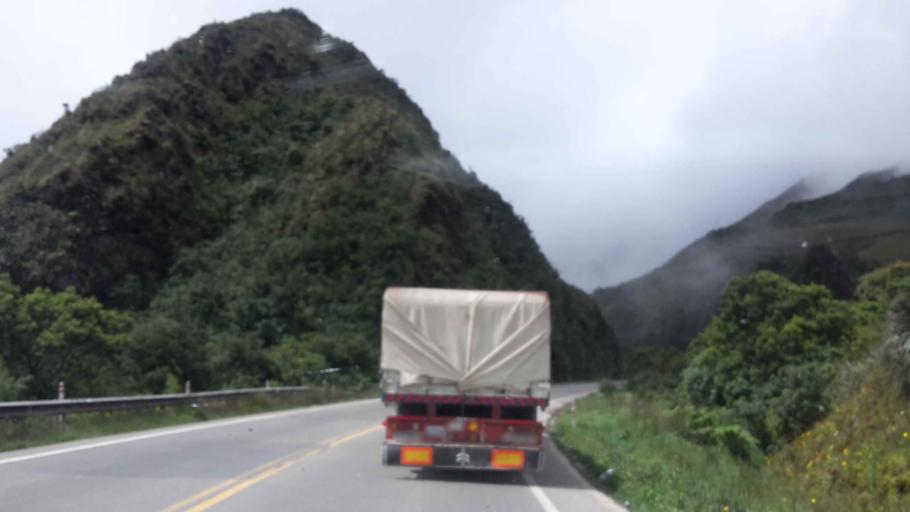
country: BO
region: Cochabamba
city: Colomi
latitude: -17.2197
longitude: -65.8938
